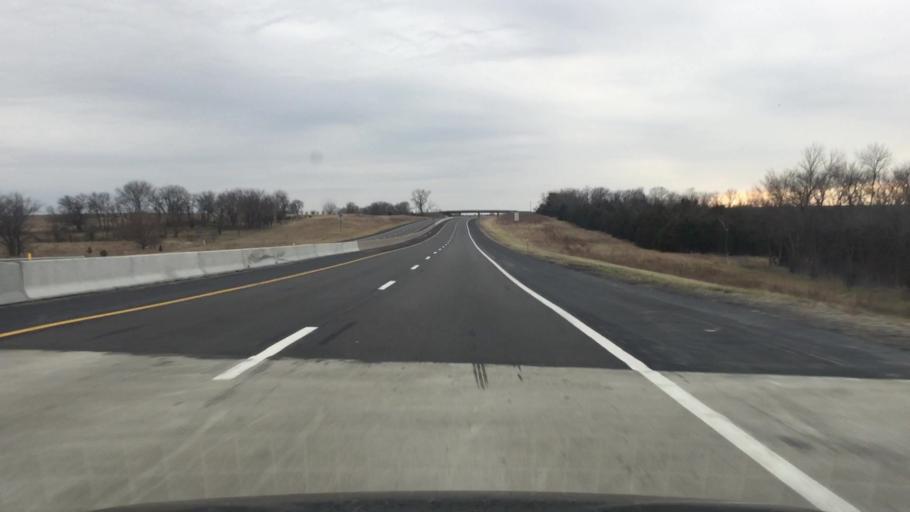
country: US
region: Kansas
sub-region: Osage County
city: Osage City
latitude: 38.7711
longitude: -95.9244
